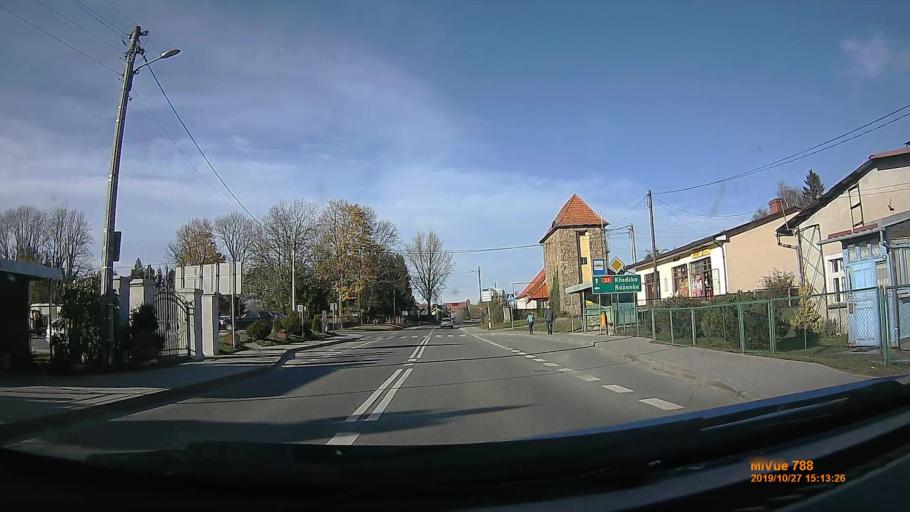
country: PL
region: Lower Silesian Voivodeship
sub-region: Powiat klodzki
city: Miedzylesie
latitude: 50.2155
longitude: 16.6804
